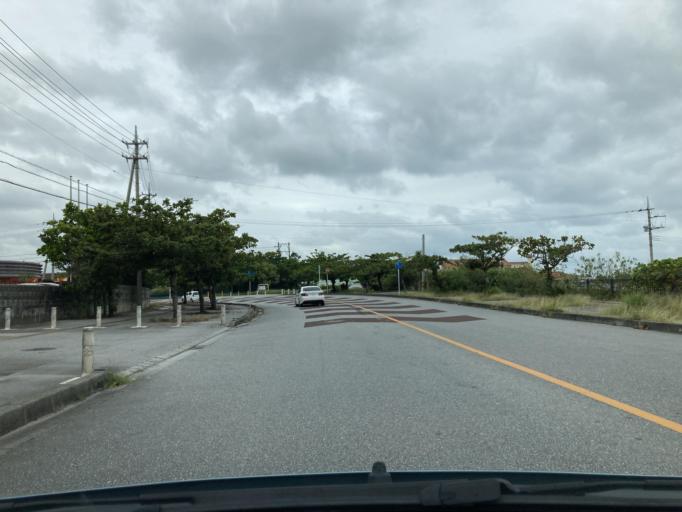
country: JP
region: Okinawa
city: Ginowan
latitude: 26.2186
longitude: 127.7772
